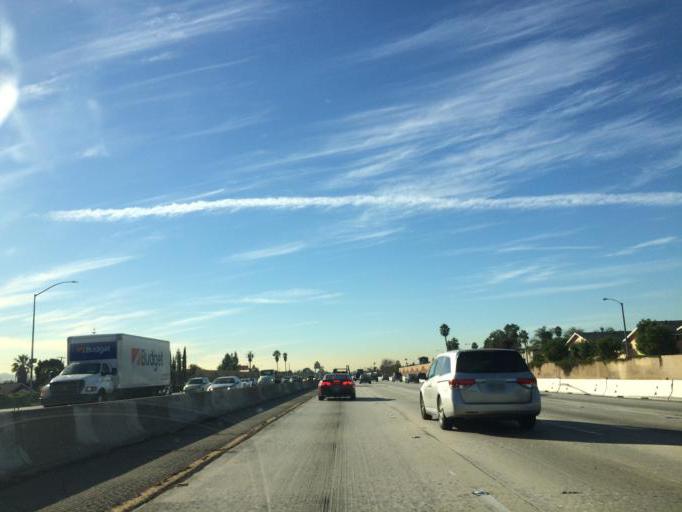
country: US
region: California
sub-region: Los Angeles County
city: Covina
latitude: 34.0720
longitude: -117.8942
